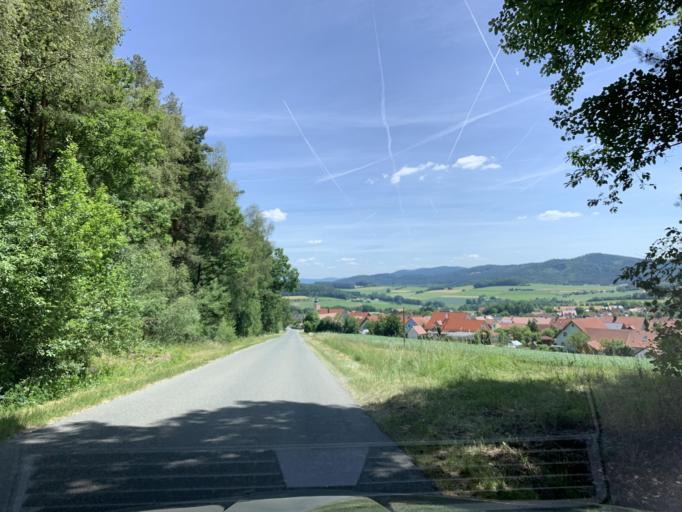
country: DE
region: Bavaria
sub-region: Upper Palatinate
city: Dieterskirchen
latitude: 49.4188
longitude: 12.4058
